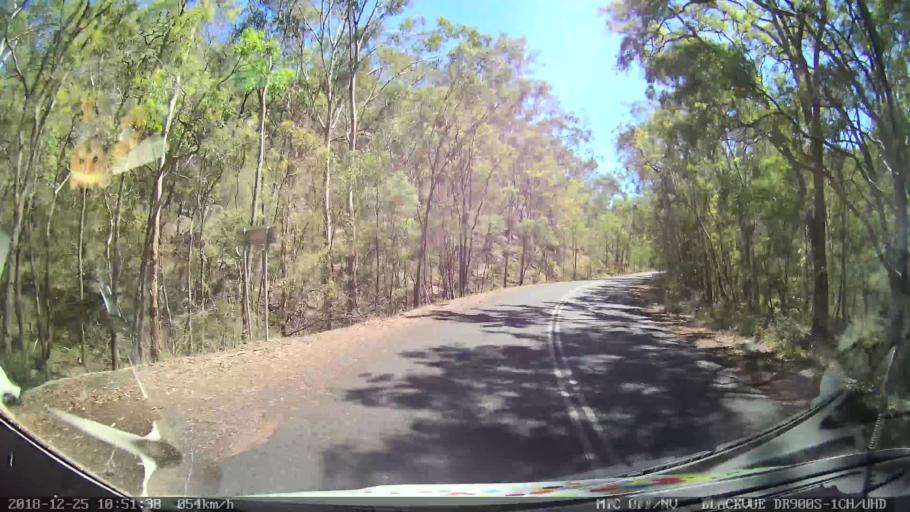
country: AU
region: New South Wales
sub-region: Upper Hunter Shire
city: Merriwa
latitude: -32.4351
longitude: 150.2695
